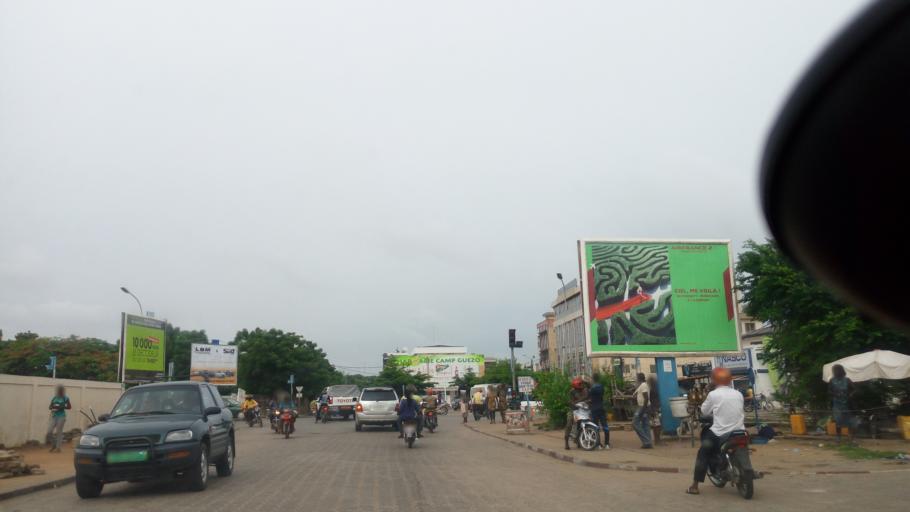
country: BJ
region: Littoral
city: Cotonou
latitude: 6.3563
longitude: 2.4169
